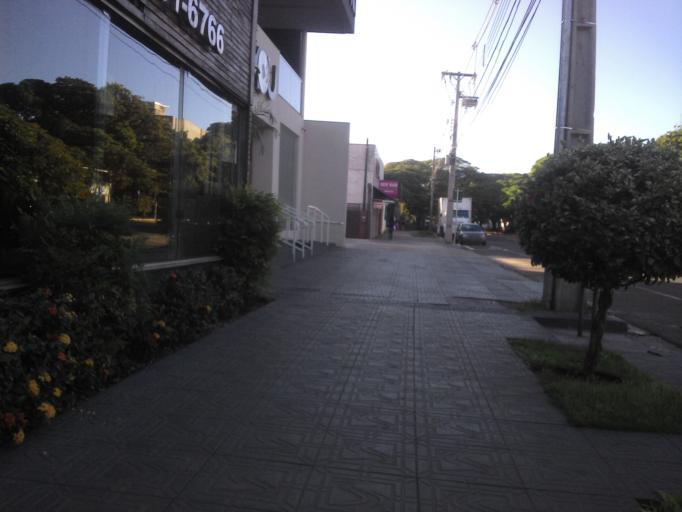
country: BR
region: Parana
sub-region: Maringa
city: Maringa
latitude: -23.4314
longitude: -51.9359
